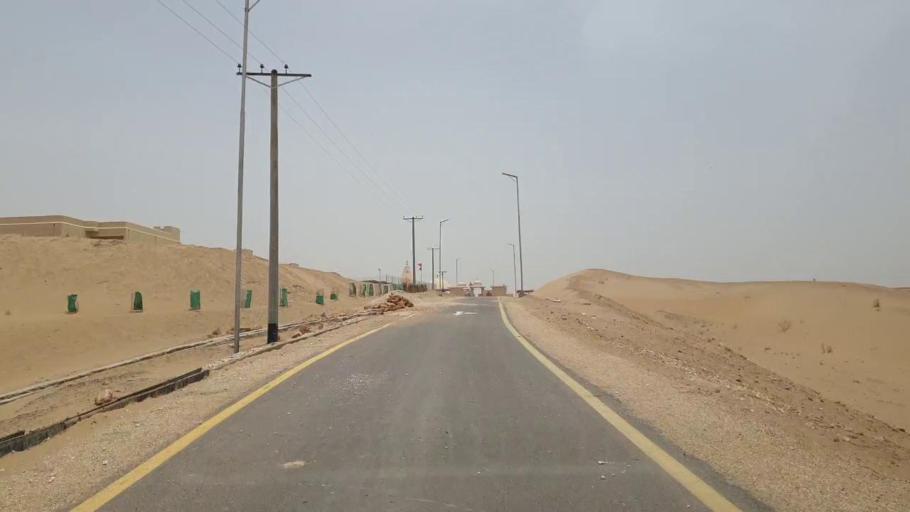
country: PK
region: Sindh
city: Islamkot
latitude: 24.7232
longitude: 70.3275
